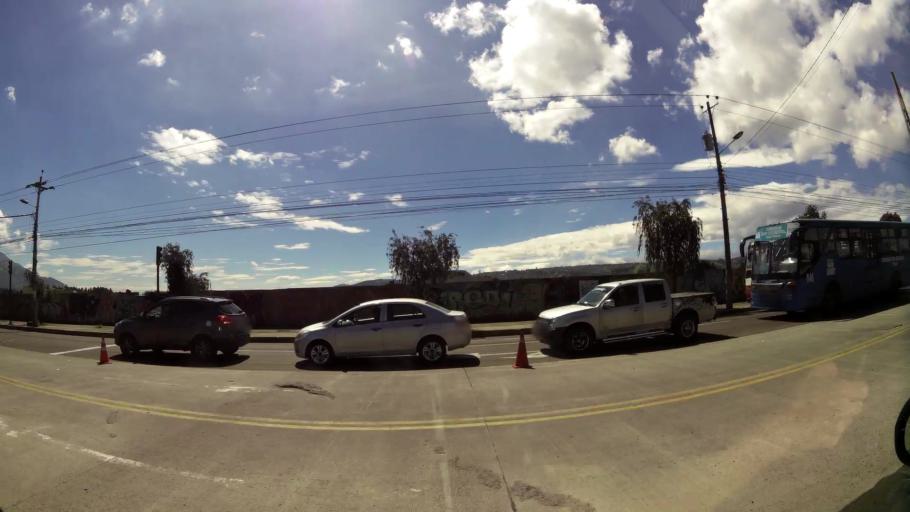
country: EC
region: Pichincha
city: Quito
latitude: -0.2942
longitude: -78.5557
